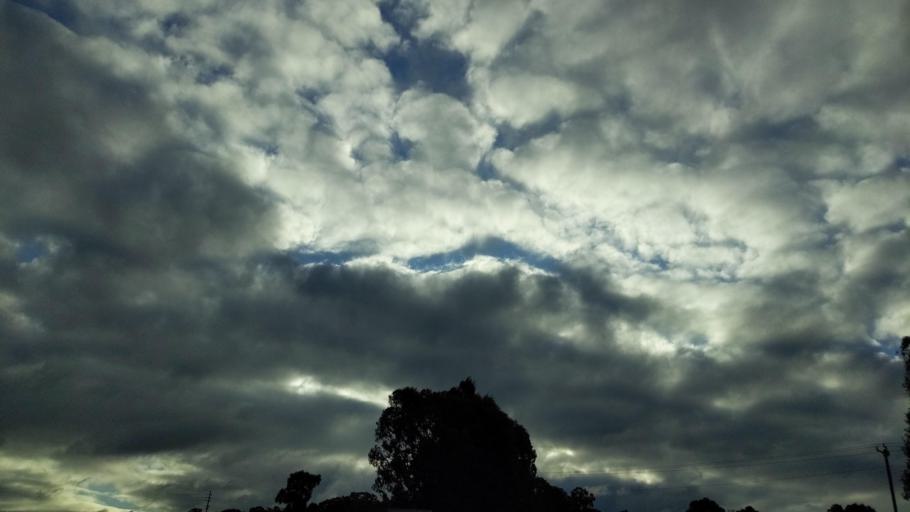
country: AU
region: New South Wales
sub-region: Wagga Wagga
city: Wagga Wagga
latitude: -35.0690
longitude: 147.3792
